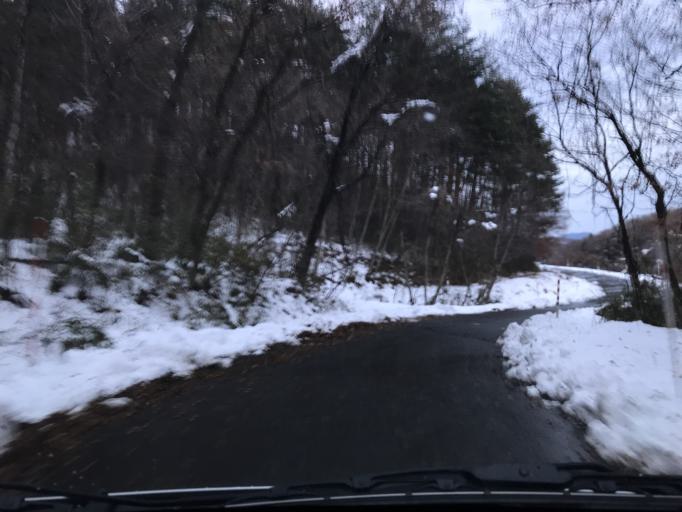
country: JP
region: Iwate
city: Mizusawa
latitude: 39.0532
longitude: 141.0260
